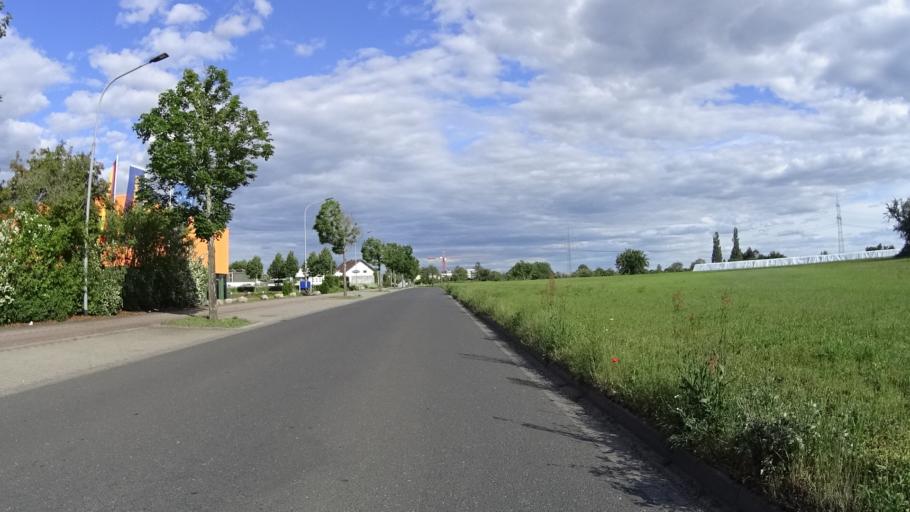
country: DE
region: Hesse
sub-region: Regierungsbezirk Darmstadt
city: Grosskrotzenburg
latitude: 50.0848
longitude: 8.9626
